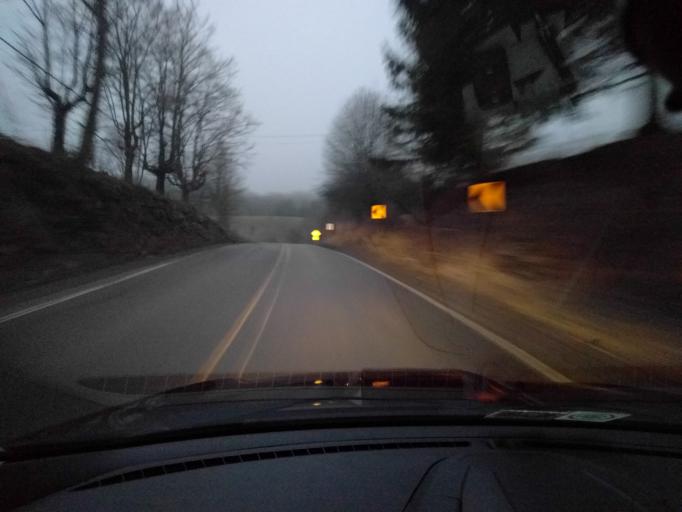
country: US
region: West Virginia
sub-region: Greenbrier County
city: Rainelle
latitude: 37.9694
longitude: -80.8074
